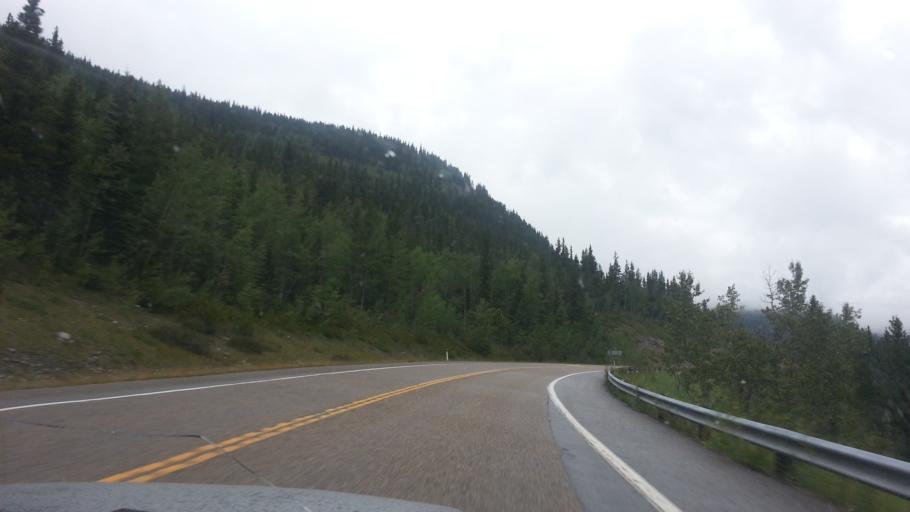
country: CA
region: Alberta
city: Cochrane
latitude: 50.8575
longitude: -114.7963
